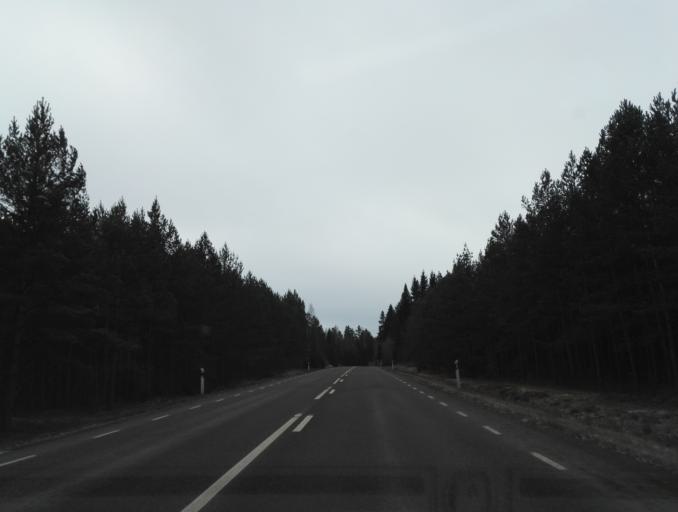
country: SE
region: Kalmar
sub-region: Hultsfreds Kommun
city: Virserum
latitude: 57.3393
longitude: 15.6032
